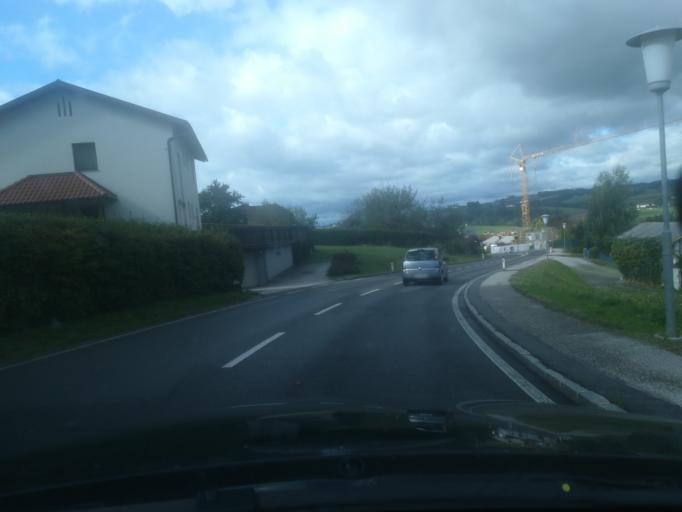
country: AT
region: Upper Austria
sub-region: Politischer Bezirk Urfahr-Umgebung
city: Gramastetten
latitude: 48.3777
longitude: 14.1987
